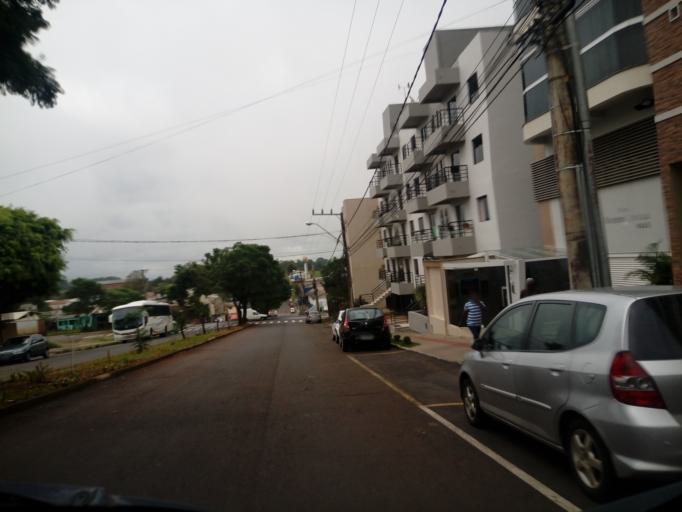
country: BR
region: Santa Catarina
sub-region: Chapeco
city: Chapeco
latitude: -27.1052
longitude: -52.6249
